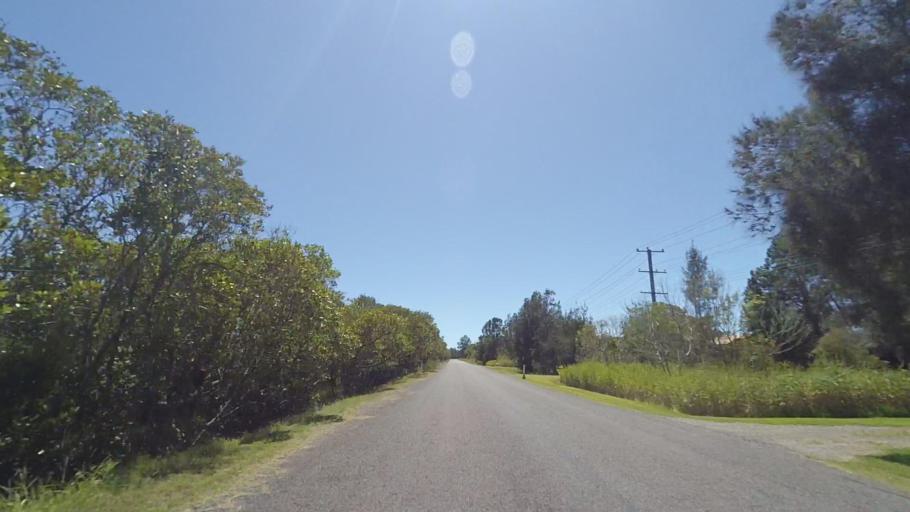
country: AU
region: New South Wales
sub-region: Port Stephens Shire
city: Medowie
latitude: -32.7816
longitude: 151.9452
